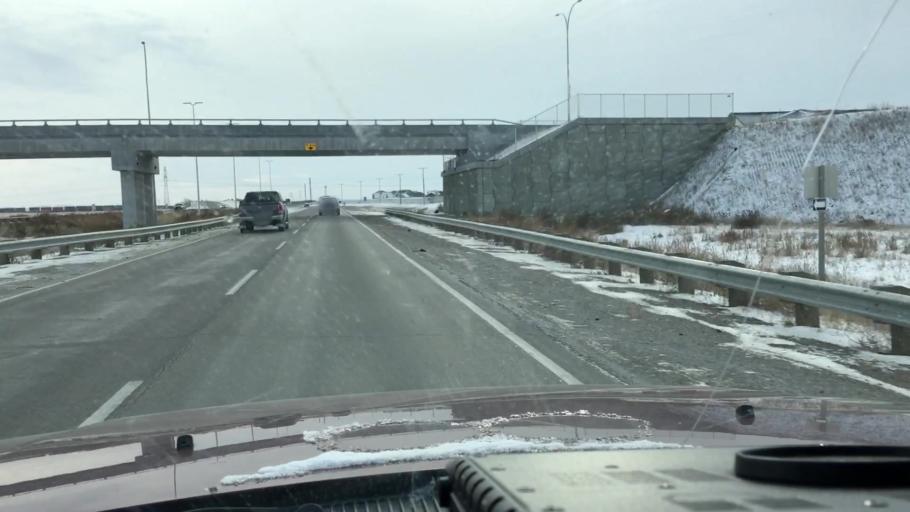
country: CA
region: Saskatchewan
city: Saskatoon
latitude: 52.0785
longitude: -106.6050
